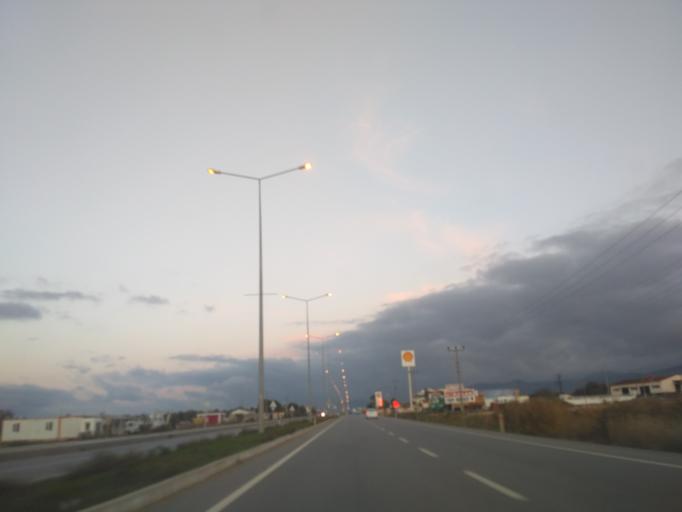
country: TR
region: Balikesir
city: Burhaniye
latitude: 39.4865
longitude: 26.9473
